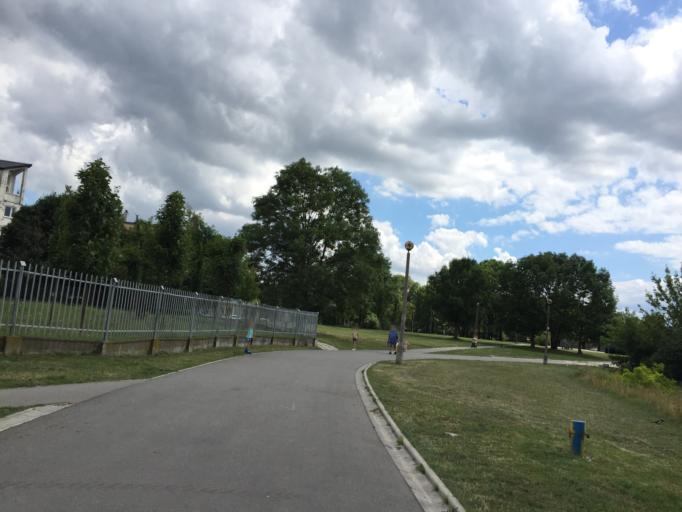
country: PL
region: Lesser Poland Voivodeship
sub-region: Powiat wielicki
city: Kokotow
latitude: 50.0678
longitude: 20.0410
